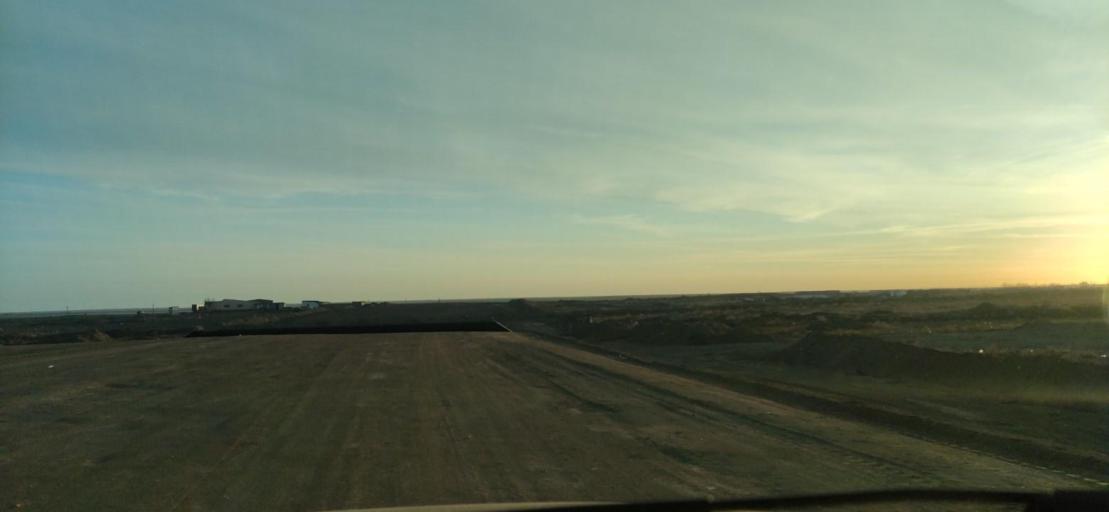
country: KZ
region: Qaraghandy
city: Saryshaghan
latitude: 46.0159
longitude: 73.5891
